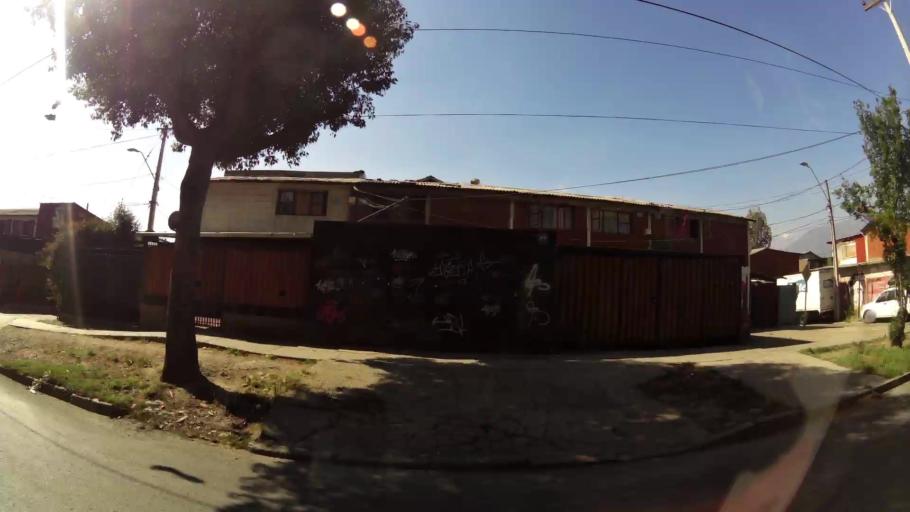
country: CL
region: Santiago Metropolitan
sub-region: Provincia de Santiago
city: Villa Presidente Frei, Nunoa, Santiago, Chile
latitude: -33.4822
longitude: -70.5710
